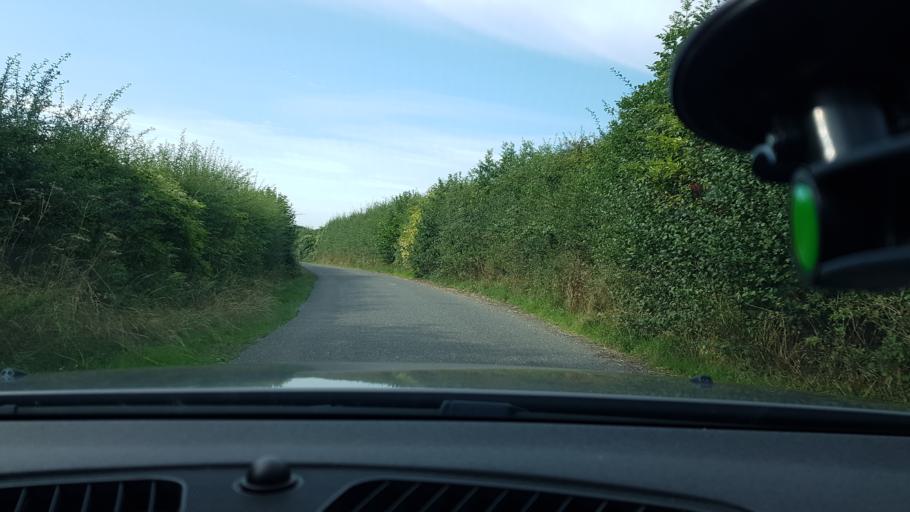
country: GB
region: England
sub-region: West Berkshire
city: Wickham
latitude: 51.4298
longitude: -1.4421
